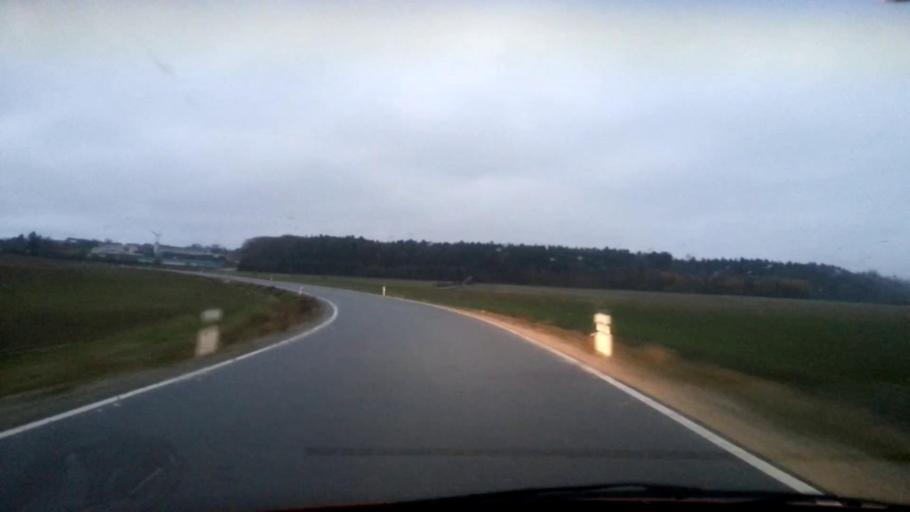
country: DE
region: Bavaria
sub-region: Upper Franconia
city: Poxdorf
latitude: 49.9648
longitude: 11.1366
